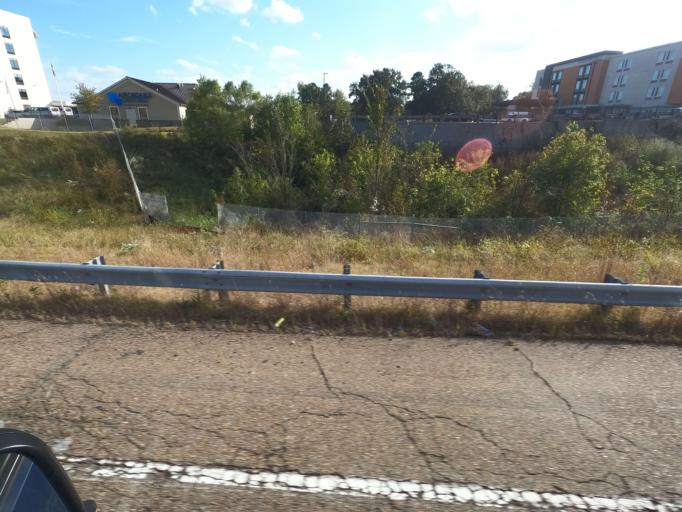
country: US
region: Tennessee
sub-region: Madison County
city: Jackson
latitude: 35.6777
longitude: -88.7854
